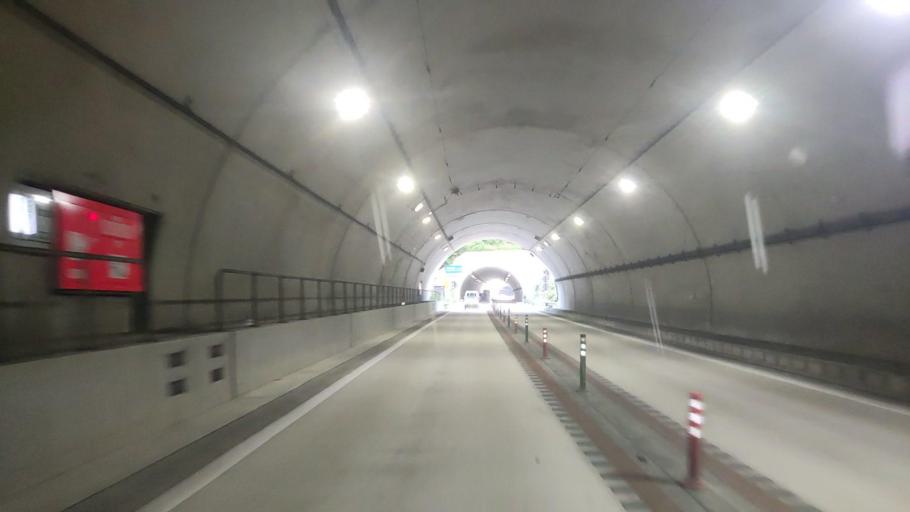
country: JP
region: Wakayama
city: Tanabe
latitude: 33.5962
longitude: 135.4347
